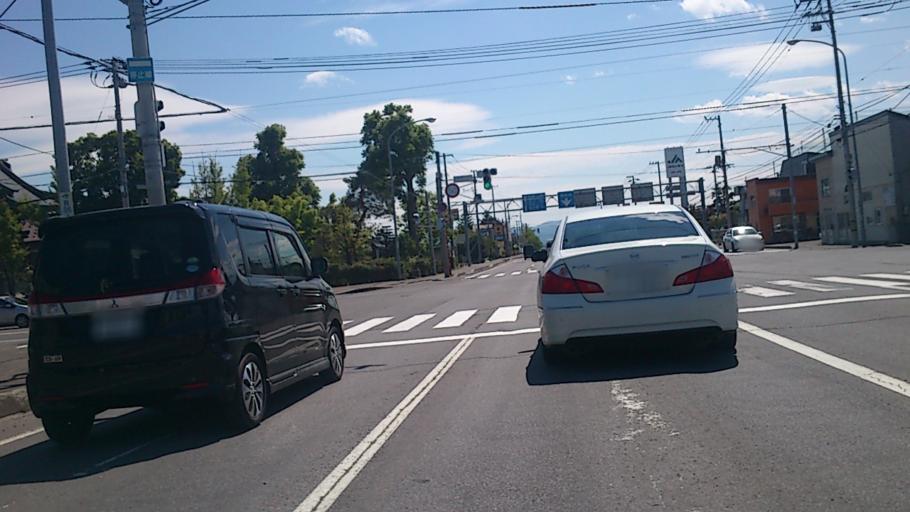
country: JP
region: Hokkaido
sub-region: Asahikawa-shi
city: Asahikawa
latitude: 43.8262
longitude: 142.4169
